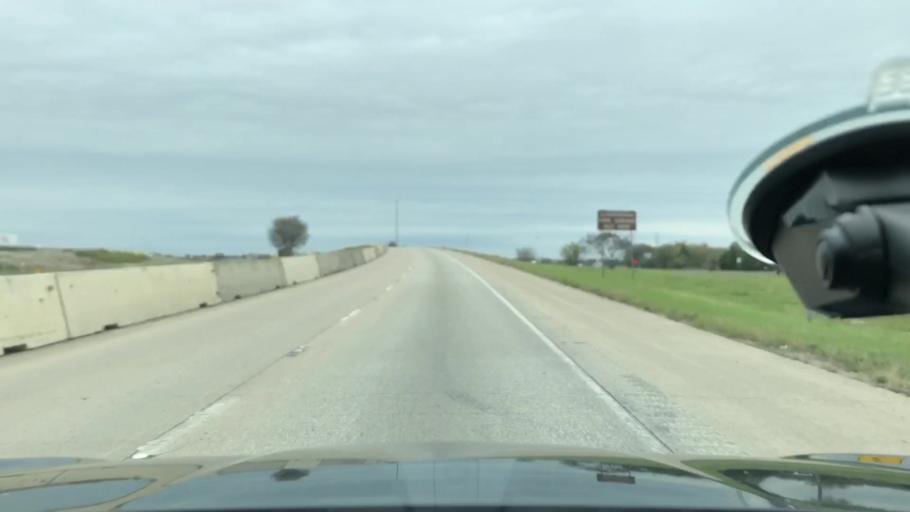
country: US
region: Texas
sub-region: Ellis County
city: Waxahachie
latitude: 32.3601
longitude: -96.8549
